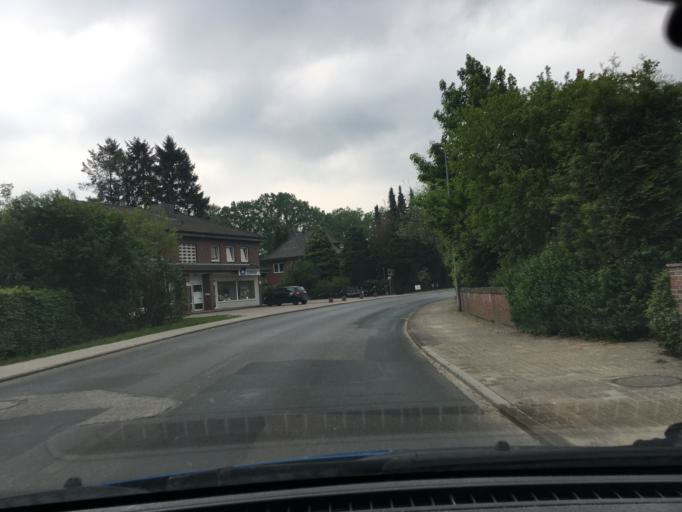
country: DE
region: Lower Saxony
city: Jesteburg
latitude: 53.3132
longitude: 9.9659
